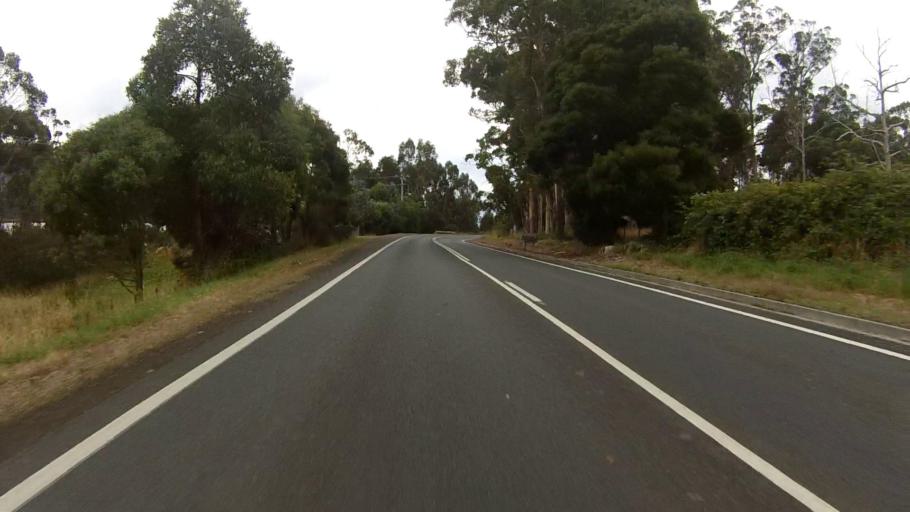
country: AU
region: Tasmania
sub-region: Huon Valley
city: Franklin
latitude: -43.0779
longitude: 147.0329
